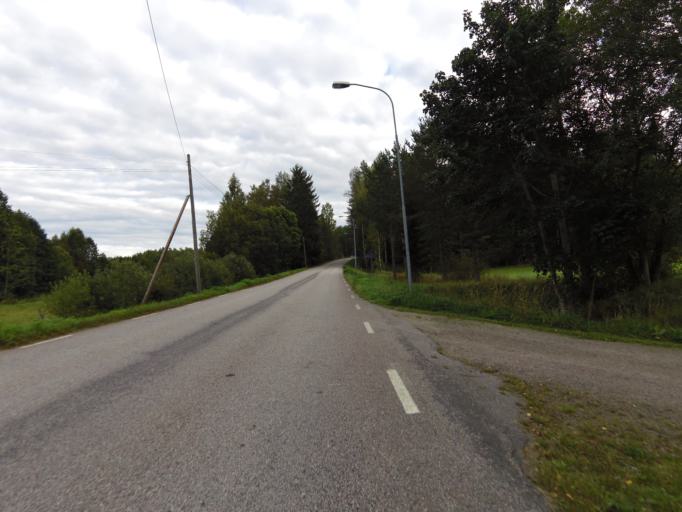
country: SE
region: Gaevleborg
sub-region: Gavle Kommun
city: Valbo
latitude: 60.6588
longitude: 16.9748
